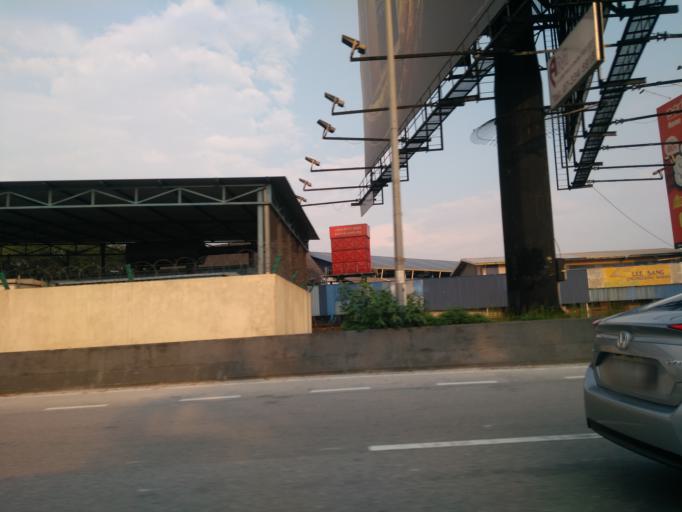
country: MY
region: Kuala Lumpur
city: Kuala Lumpur
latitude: 3.1137
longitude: 101.7056
